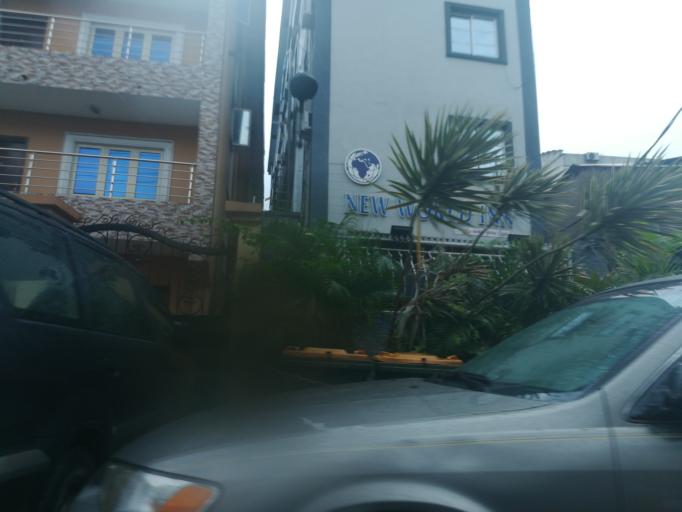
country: NG
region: Lagos
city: Lagos
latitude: 6.4501
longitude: 3.4029
